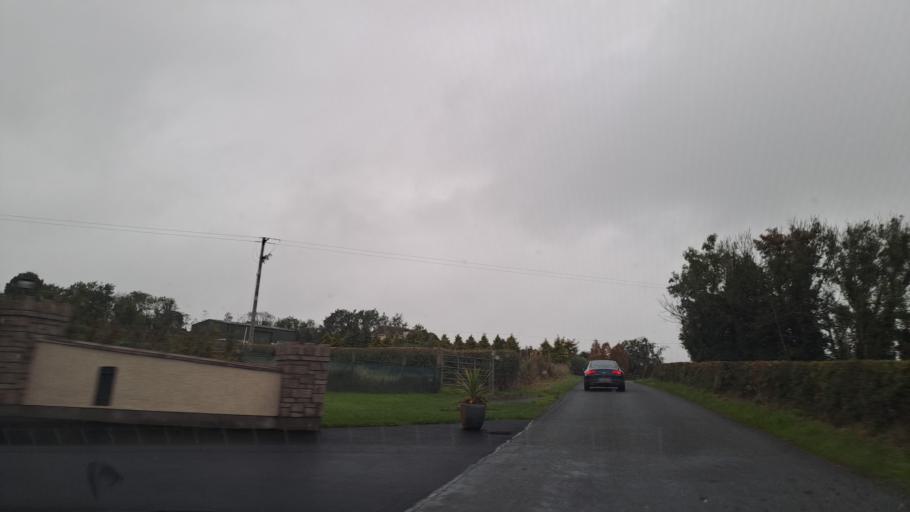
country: IE
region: Ulster
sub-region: County Monaghan
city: Monaghan
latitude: 54.2097
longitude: -6.9086
